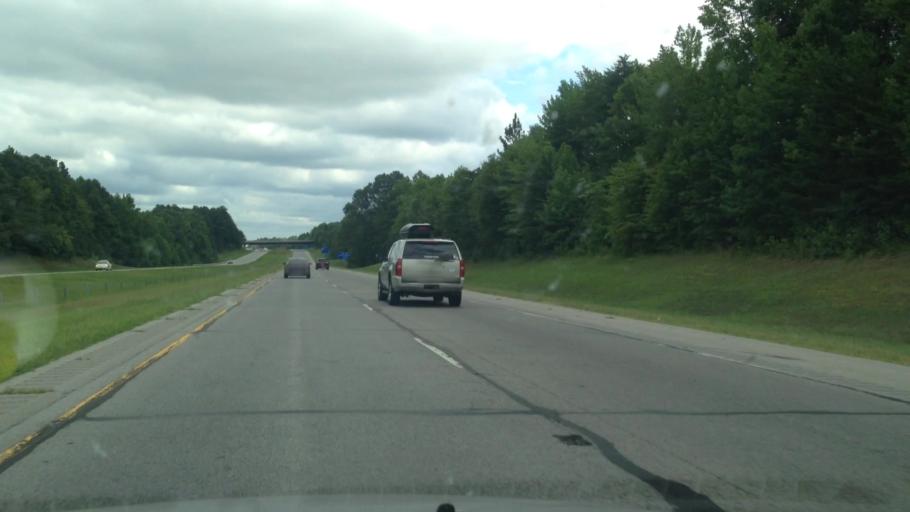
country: US
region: Virginia
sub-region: City of Danville
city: Danville
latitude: 36.5021
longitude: -79.4809
